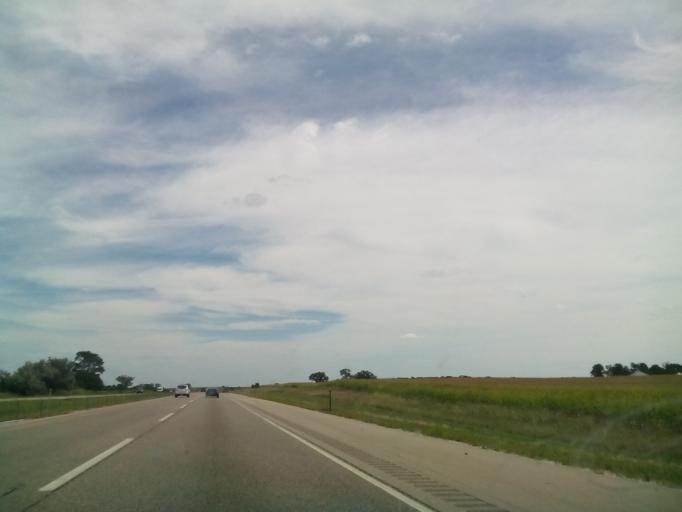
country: US
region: Illinois
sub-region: Kane County
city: Maple Park
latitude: 41.8669
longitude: -88.5737
